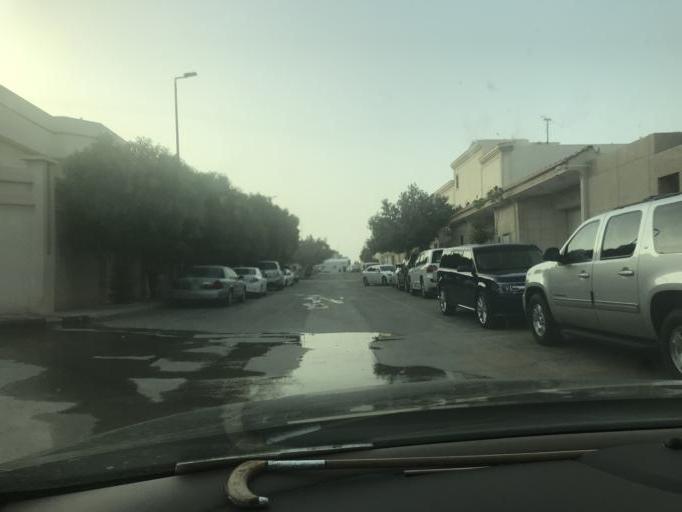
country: SA
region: Ar Riyad
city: Riyadh
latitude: 24.7401
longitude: 46.7554
